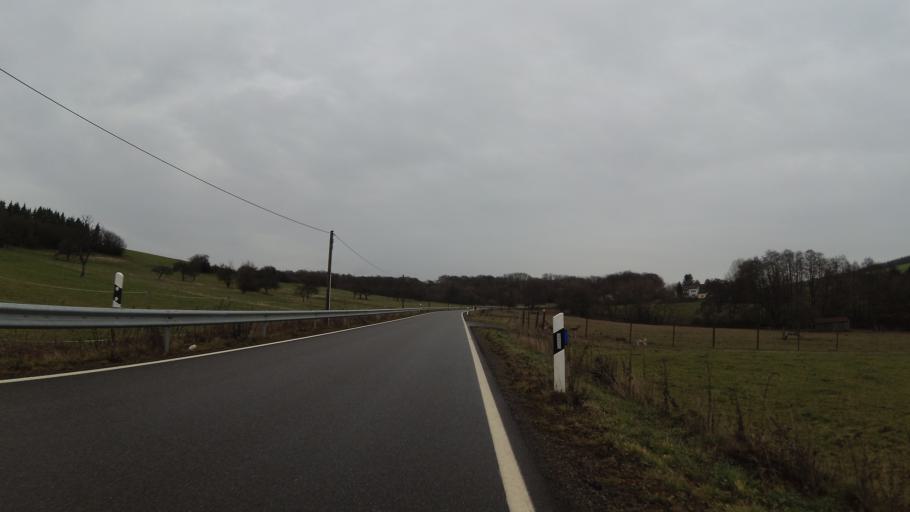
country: DE
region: Rheinland-Pfalz
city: Breitenbach
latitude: 49.4444
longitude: 7.2790
